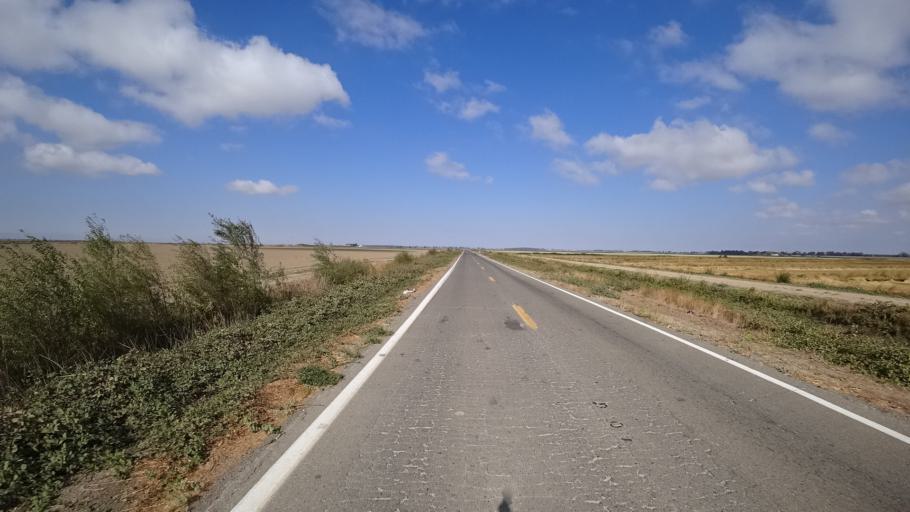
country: US
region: California
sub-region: Yolo County
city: Woodland
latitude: 38.8144
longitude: -121.7383
